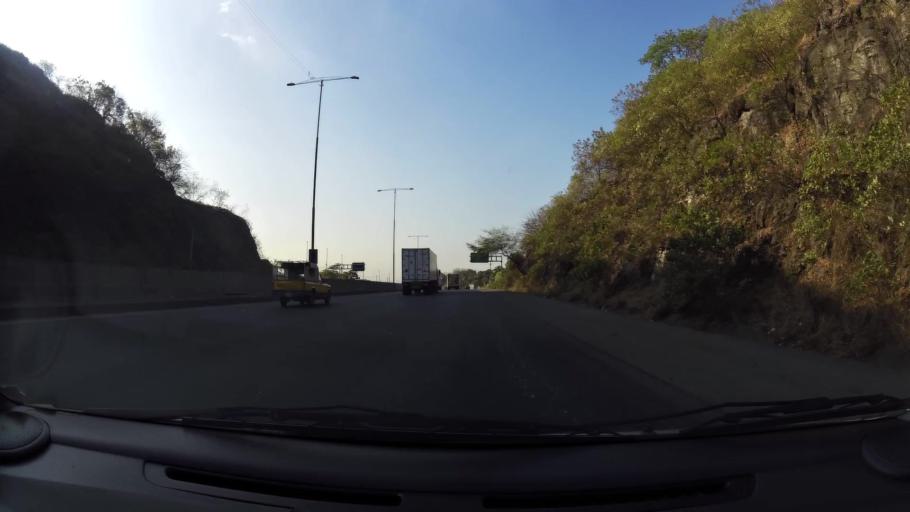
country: EC
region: Guayas
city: Santa Lucia
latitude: -2.1526
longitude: -79.9467
